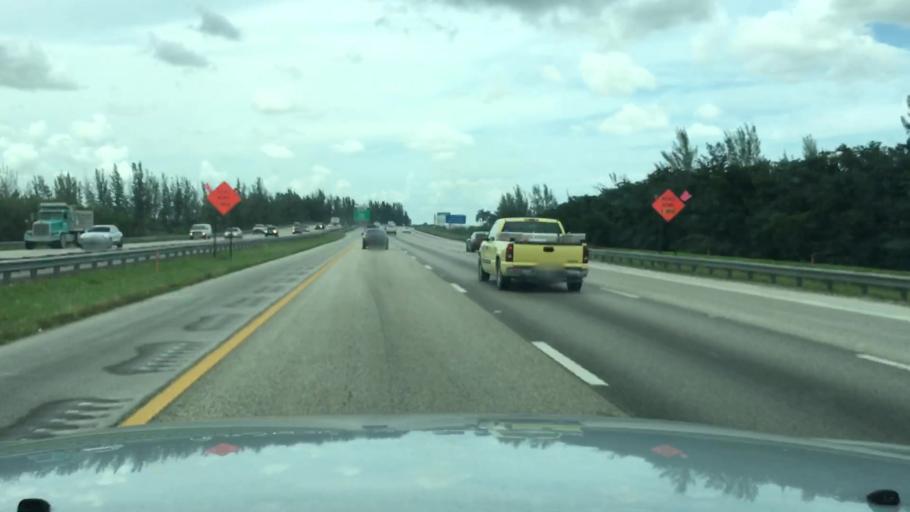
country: US
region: Florida
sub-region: Miami-Dade County
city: Palm Springs North
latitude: 25.9210
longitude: -80.3771
